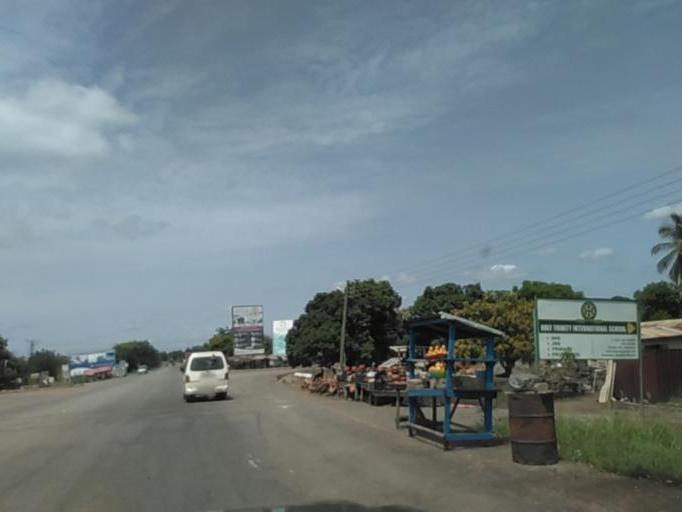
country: GH
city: Akropong
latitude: 6.0945
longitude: 0.0443
